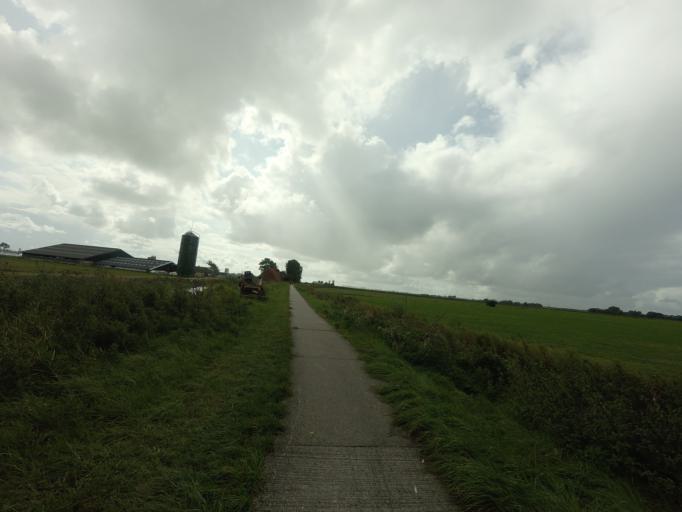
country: NL
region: Friesland
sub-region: Gemeente Boarnsterhim
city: Wergea
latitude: 53.1459
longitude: 5.8245
